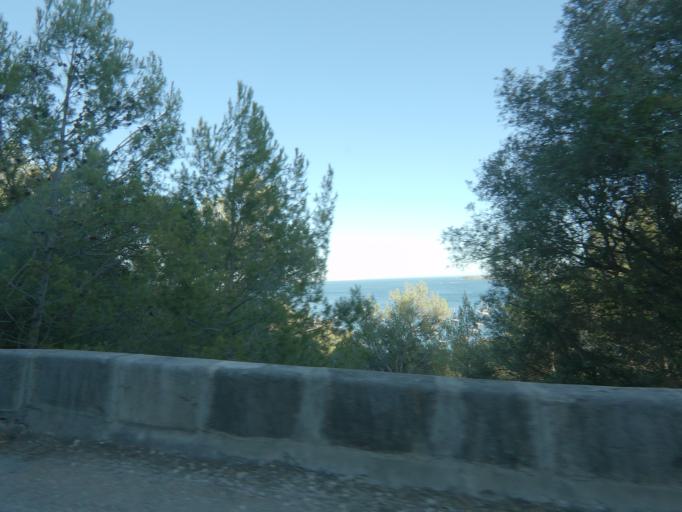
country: PT
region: Setubal
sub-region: Setubal
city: Setubal
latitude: 38.5103
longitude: -8.9218
